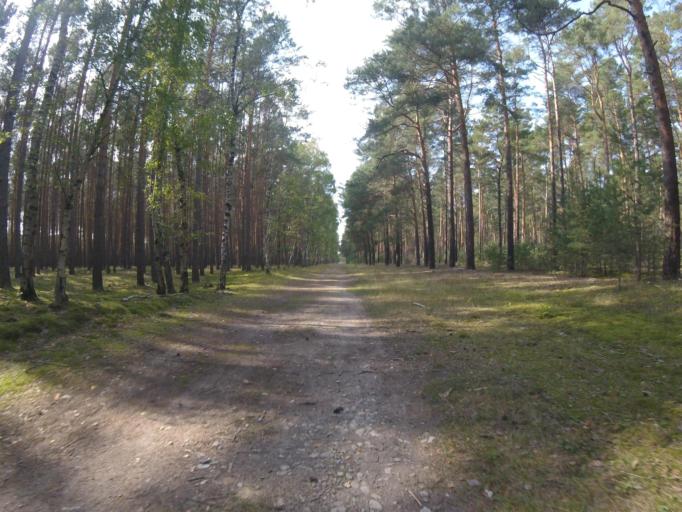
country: DE
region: Brandenburg
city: Gross Koris
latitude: 52.2235
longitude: 13.7413
